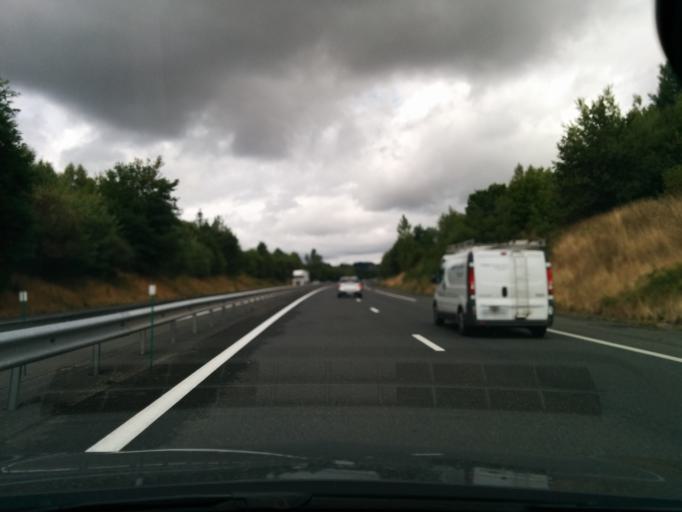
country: FR
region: Limousin
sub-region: Departement de la Correze
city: Vigeois
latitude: 45.4164
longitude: 1.5204
